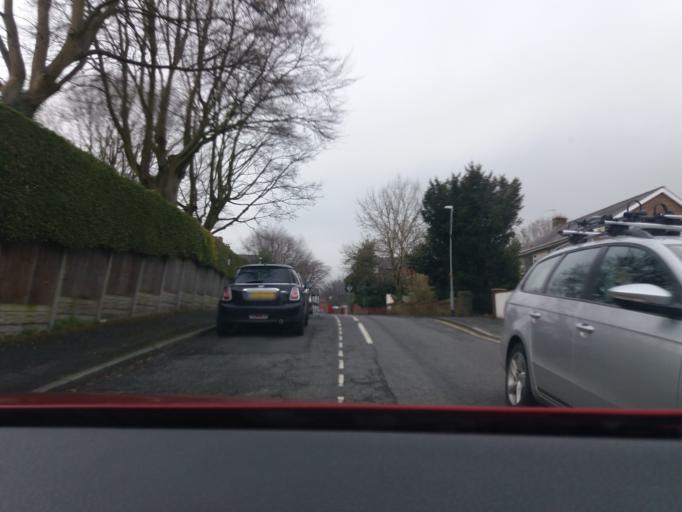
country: GB
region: England
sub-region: Lancashire
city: Chorley
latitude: 53.6546
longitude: -2.6377
